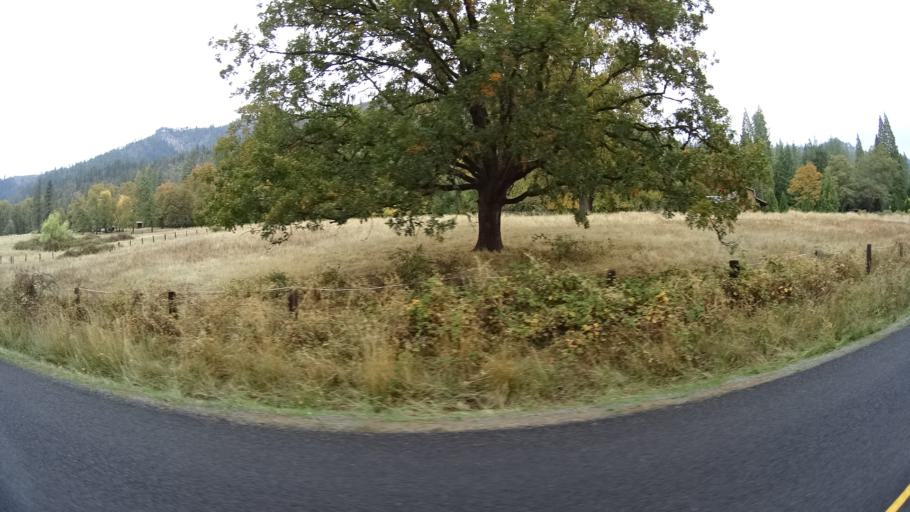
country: US
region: California
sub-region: Siskiyou County
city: Happy Camp
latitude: 41.8461
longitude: -123.1902
